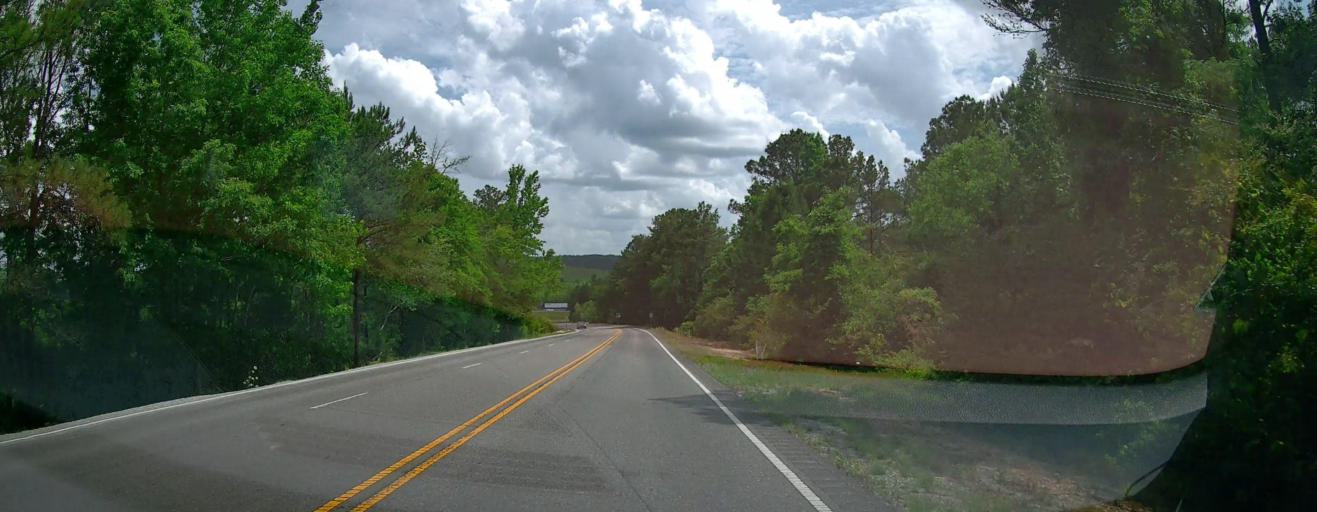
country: US
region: Alabama
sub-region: Marion County
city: Hamilton
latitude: 34.0769
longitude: -87.9769
